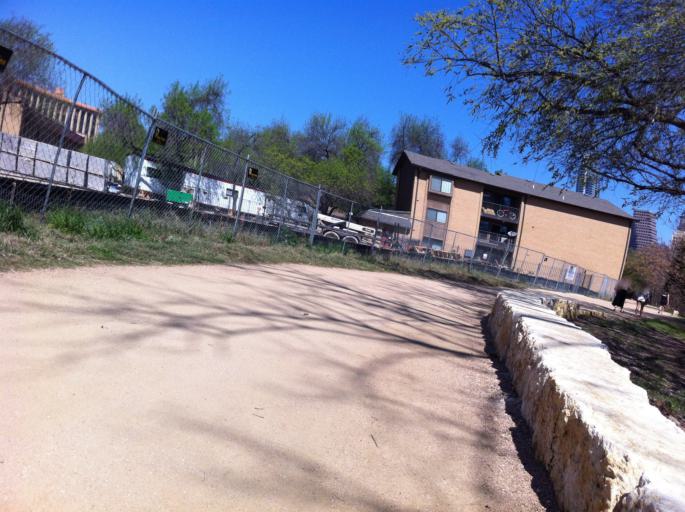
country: US
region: Texas
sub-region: Travis County
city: Austin
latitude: 30.2547
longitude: -97.7426
